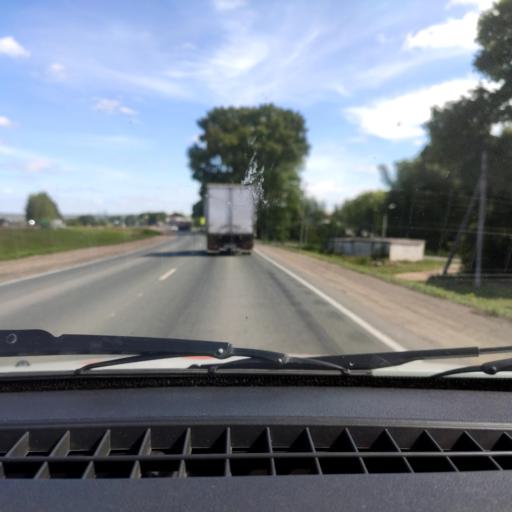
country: RU
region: Bashkortostan
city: Blagoveshchensk
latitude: 55.0566
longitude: 55.9448
